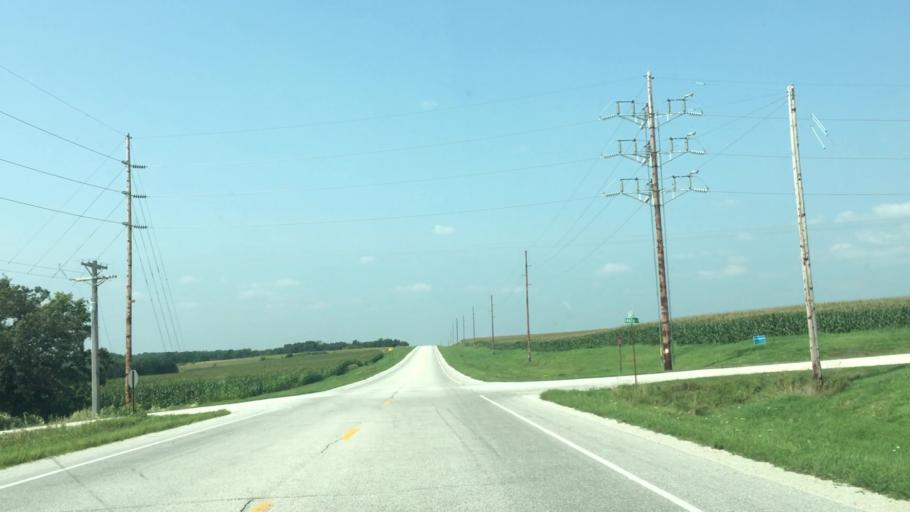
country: US
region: Minnesota
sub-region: Fillmore County
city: Harmony
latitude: 43.5655
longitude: -91.9298
